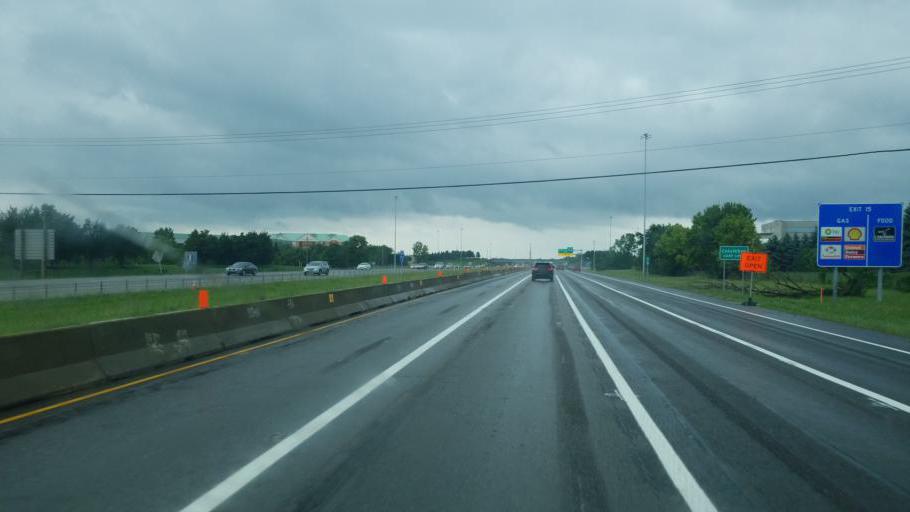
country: US
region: Ohio
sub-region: Franklin County
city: Dublin
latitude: 40.0816
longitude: -83.1374
